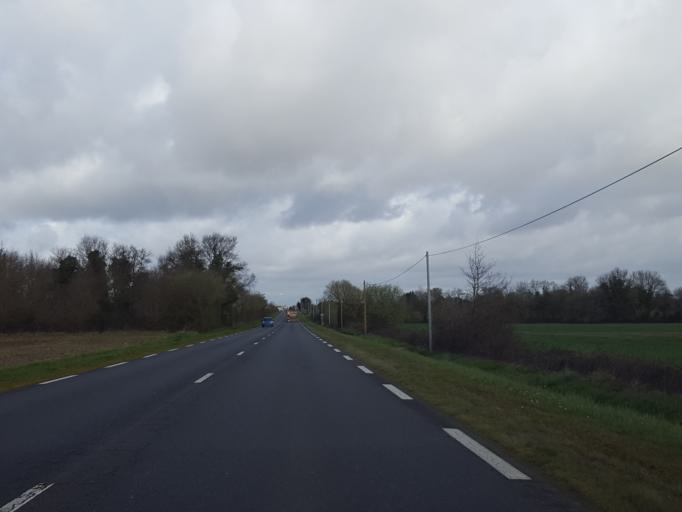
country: FR
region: Pays de la Loire
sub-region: Departement de la Loire-Atlantique
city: Le Bignon
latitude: 47.1008
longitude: -1.5343
